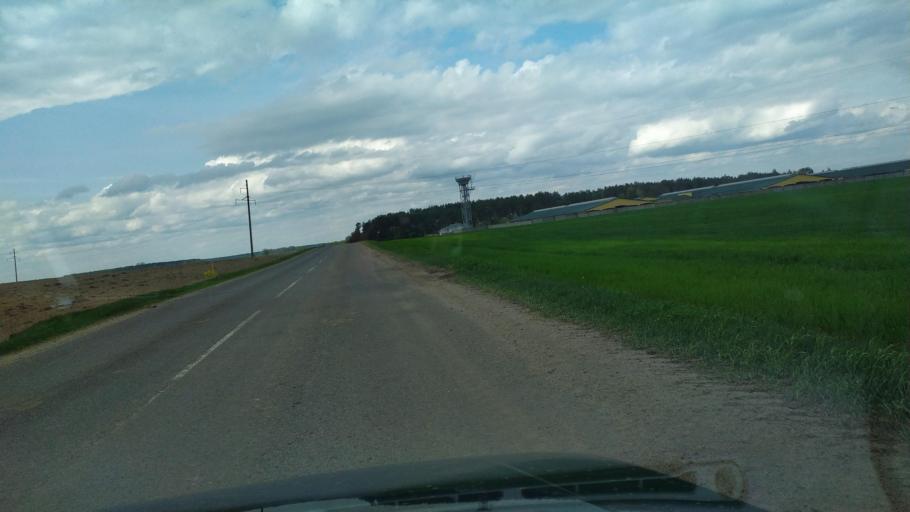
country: BY
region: Brest
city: Pruzhany
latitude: 52.6383
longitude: 24.3833
